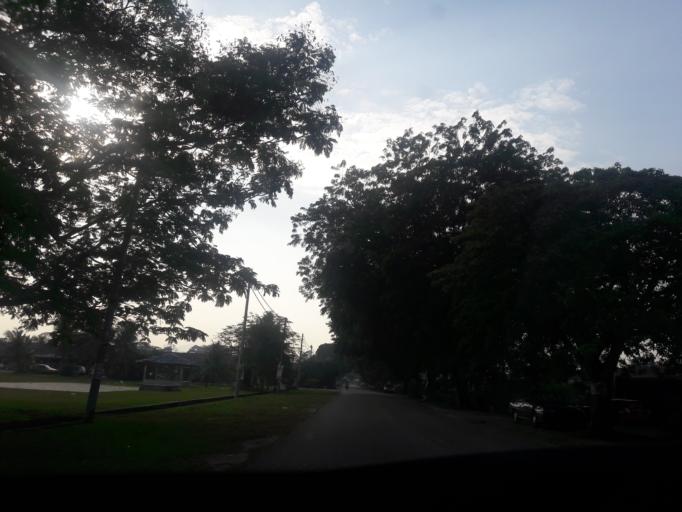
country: MY
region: Kedah
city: Kulim
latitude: 5.3755
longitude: 100.5288
